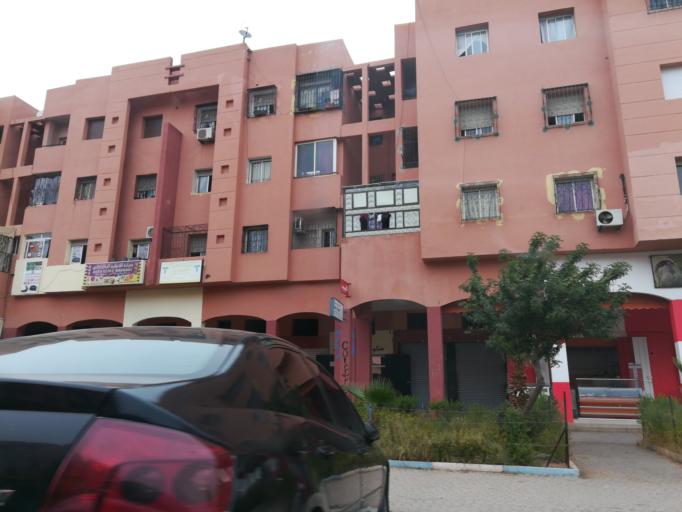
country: MA
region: Marrakech-Tensift-Al Haouz
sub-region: Marrakech
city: Marrakesh
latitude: 31.5732
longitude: -8.0560
